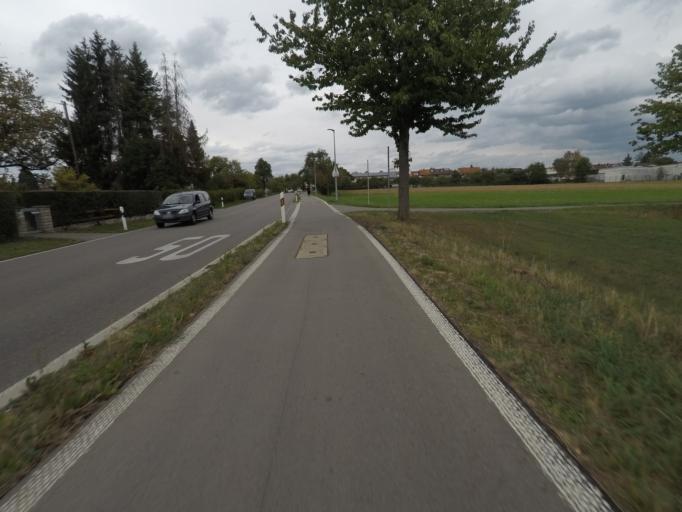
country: DE
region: Baden-Wuerttemberg
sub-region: Regierungsbezirk Stuttgart
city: Leinfelden-Echterdingen
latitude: 48.6801
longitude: 9.1671
